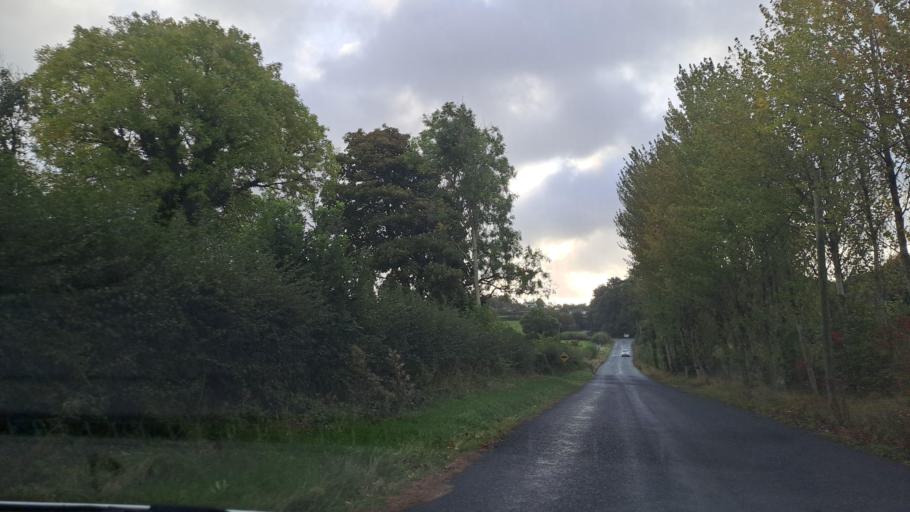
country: IE
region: Ulster
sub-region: An Cabhan
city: Kingscourt
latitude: 53.9483
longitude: -6.7688
